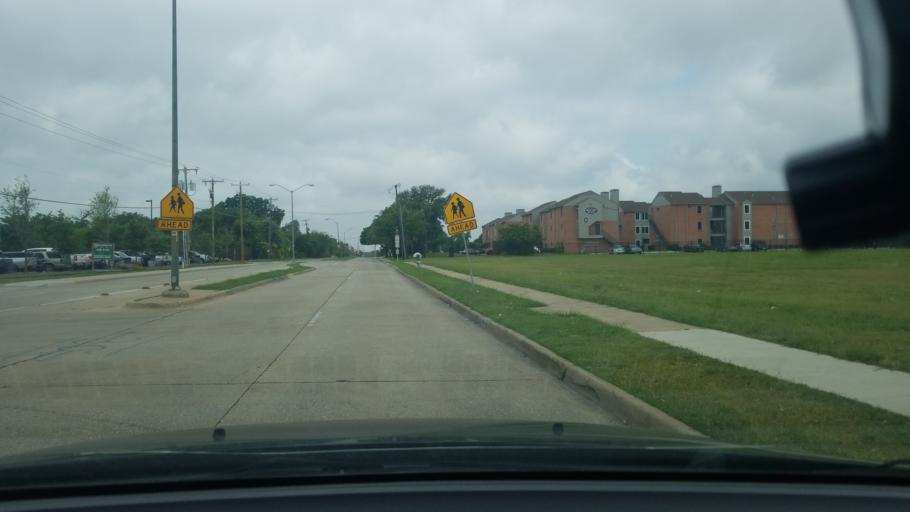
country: US
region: Texas
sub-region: Dallas County
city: Balch Springs
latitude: 32.7781
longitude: -96.6845
